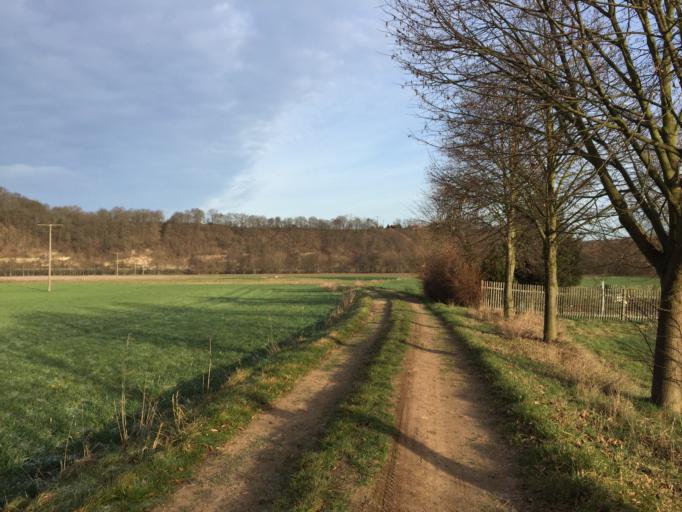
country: DE
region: Thuringia
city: Grosseutersdorf
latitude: 50.7905
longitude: 11.5732
